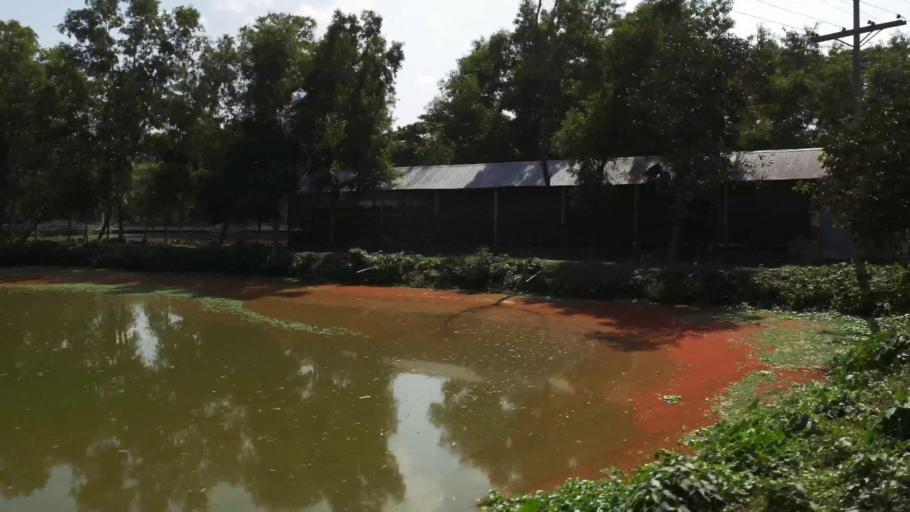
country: BD
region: Dhaka
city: Gafargaon
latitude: 24.2224
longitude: 90.4867
